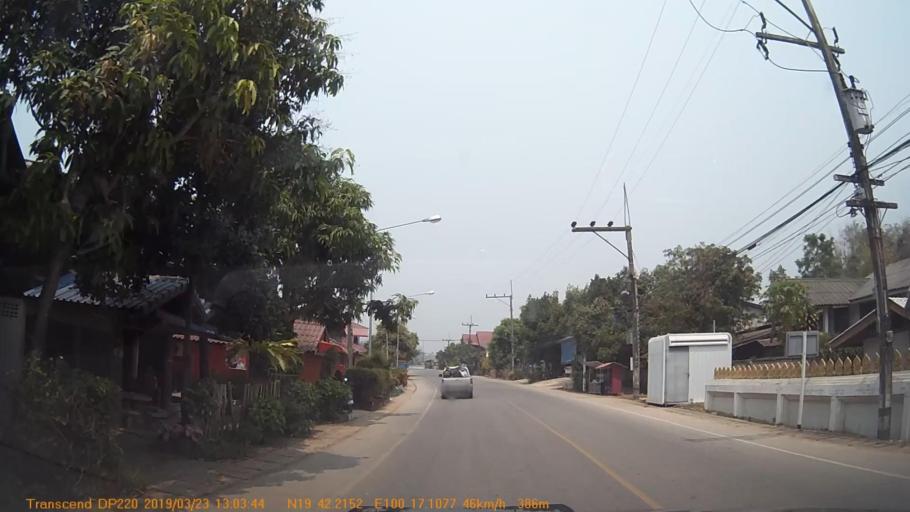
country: TH
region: Chiang Rai
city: Thoeng
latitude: 19.7038
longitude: 100.2852
